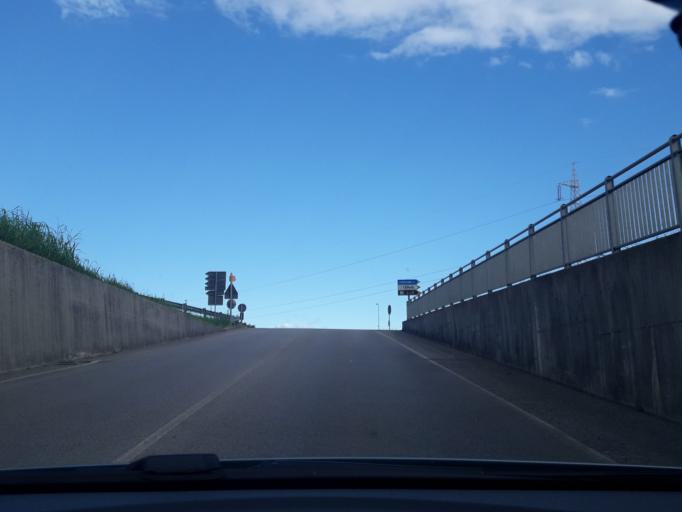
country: IT
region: Friuli Venezia Giulia
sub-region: Provincia di Udine
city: Passons
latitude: 46.0613
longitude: 13.1883
